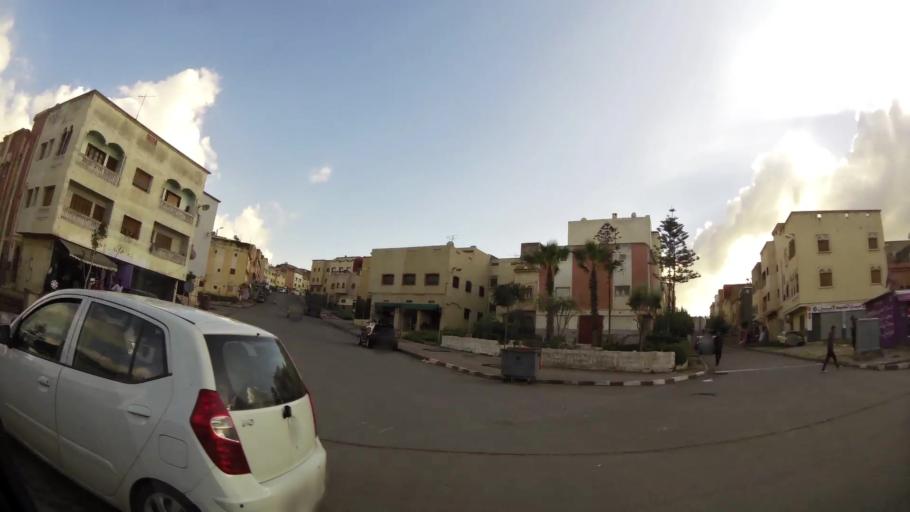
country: MA
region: Chaouia-Ouardigha
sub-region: Settat Province
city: Settat
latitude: 33.0087
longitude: -7.6292
